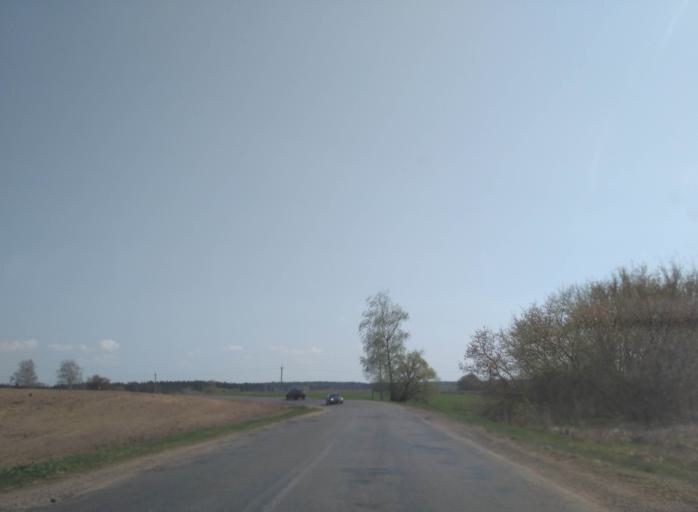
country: BY
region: Minsk
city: Horad Barysaw
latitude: 54.3146
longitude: 28.5536
